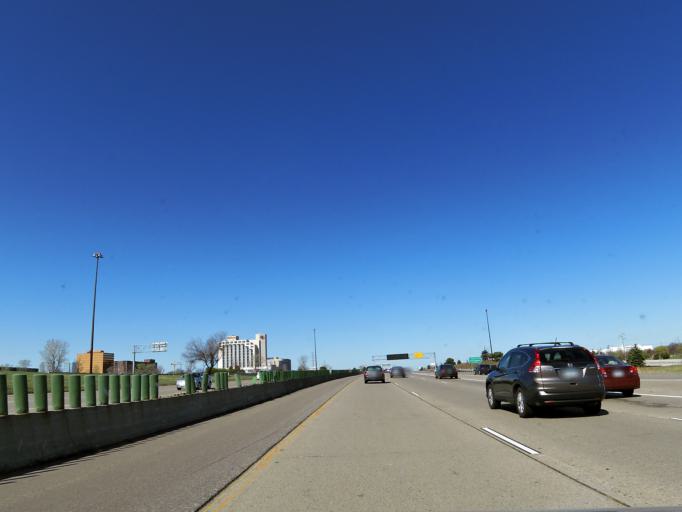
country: US
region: Minnesota
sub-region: Hennepin County
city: Richfield
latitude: 44.8623
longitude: -93.2126
